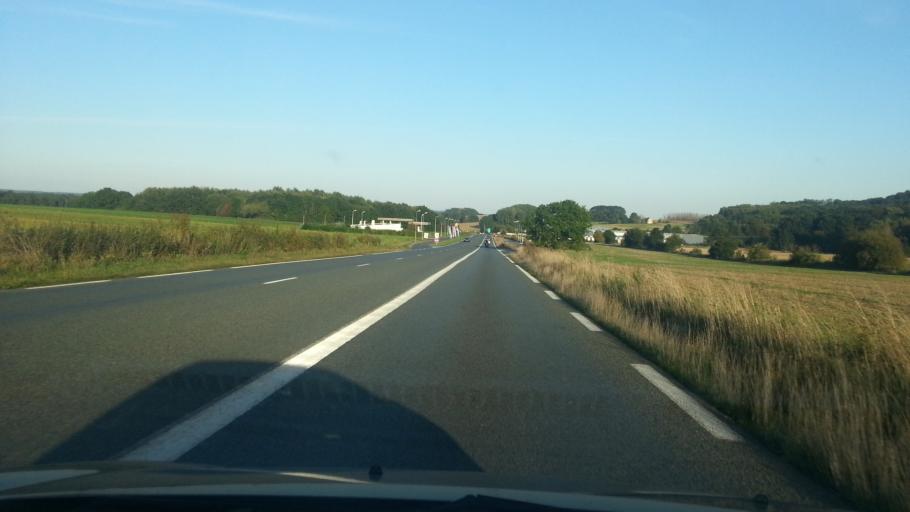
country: FR
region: Picardie
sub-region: Departement de l'Oise
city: Remy
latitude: 49.4026
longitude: 2.7318
